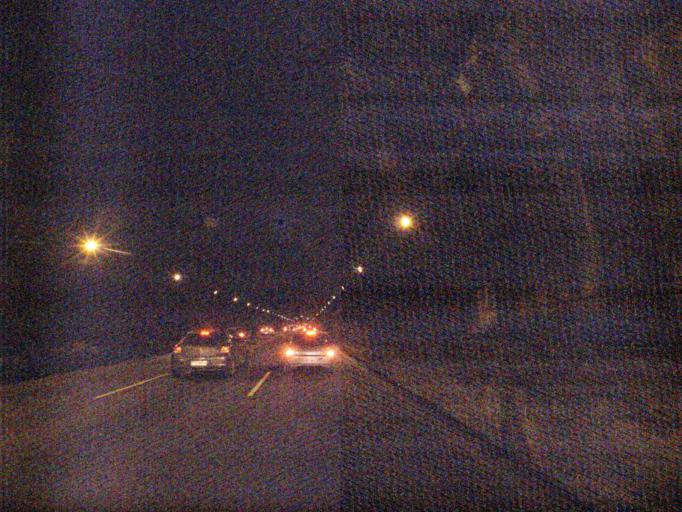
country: BR
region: Rio de Janeiro
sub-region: Rio De Janeiro
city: Rio de Janeiro
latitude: -22.9429
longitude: -43.2026
